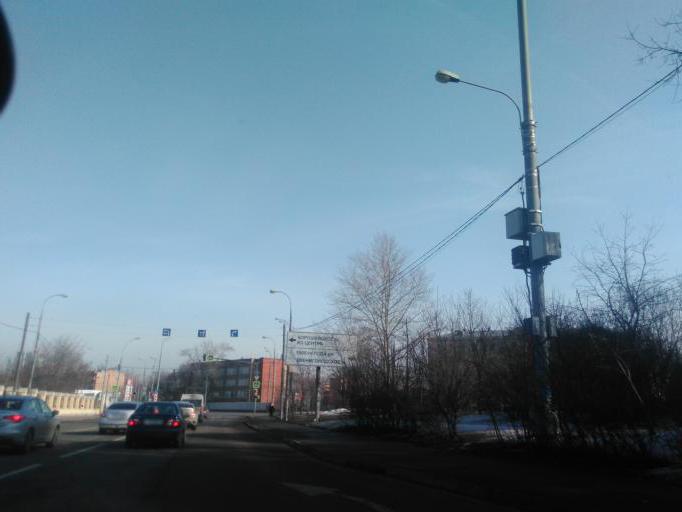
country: RU
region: Moskovskaya
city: Presnenskiy
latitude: 55.7684
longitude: 37.5554
